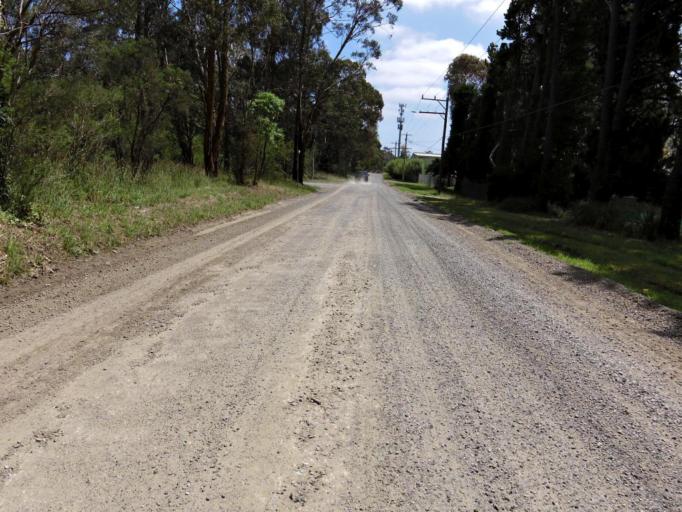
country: AU
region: Victoria
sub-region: Knox
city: Wantirna South
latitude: -37.8796
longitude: 145.1997
